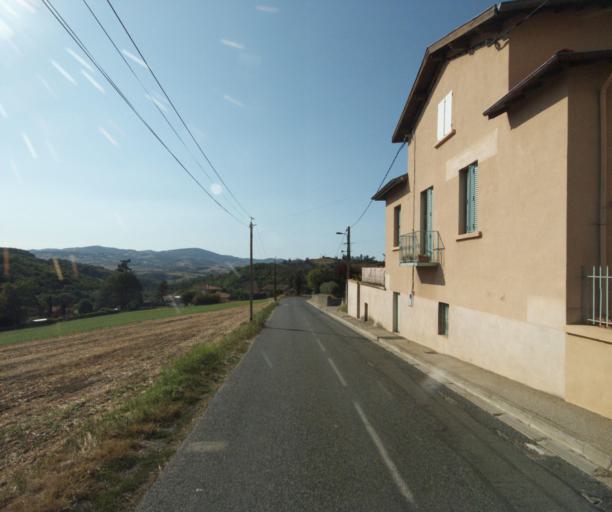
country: FR
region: Rhone-Alpes
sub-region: Departement du Rhone
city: Saint-Pierre-la-Palud
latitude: 45.7853
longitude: 4.6150
